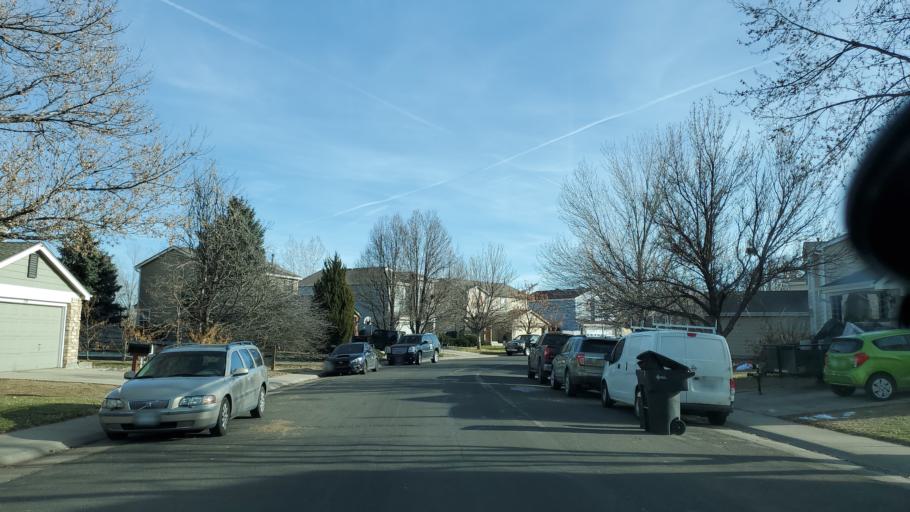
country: US
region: Colorado
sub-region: Adams County
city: Northglenn
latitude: 39.9112
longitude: -104.9526
